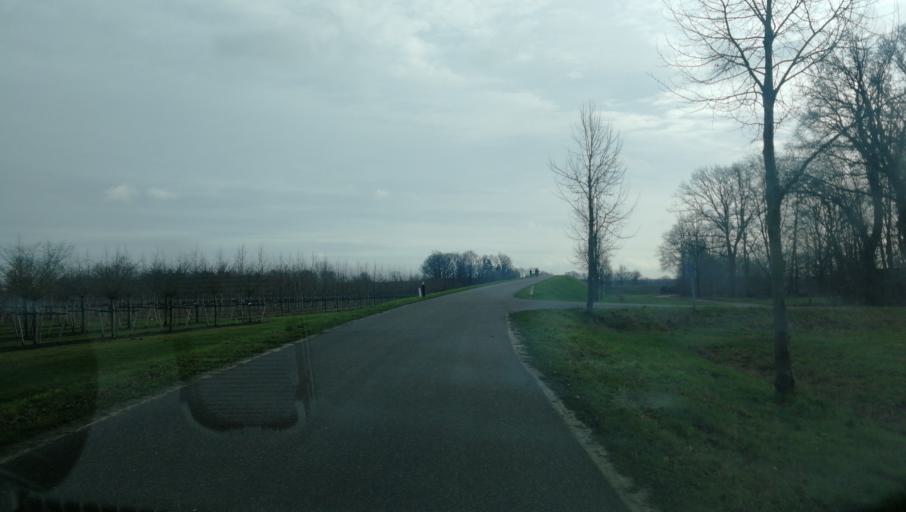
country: NL
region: Limburg
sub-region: Gemeente Beesel
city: Offenbeek
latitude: 51.2962
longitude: 6.1015
